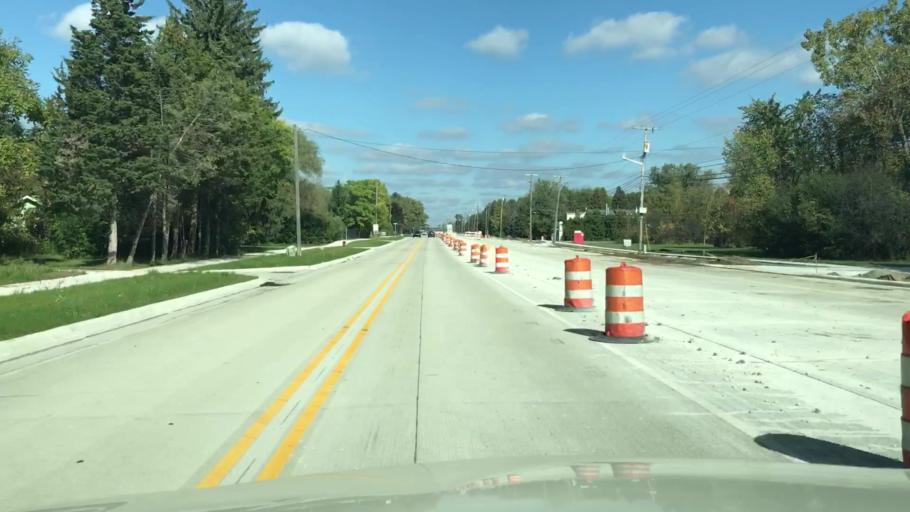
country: US
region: Michigan
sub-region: Oakland County
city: Troy
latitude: 42.5997
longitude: -83.0903
